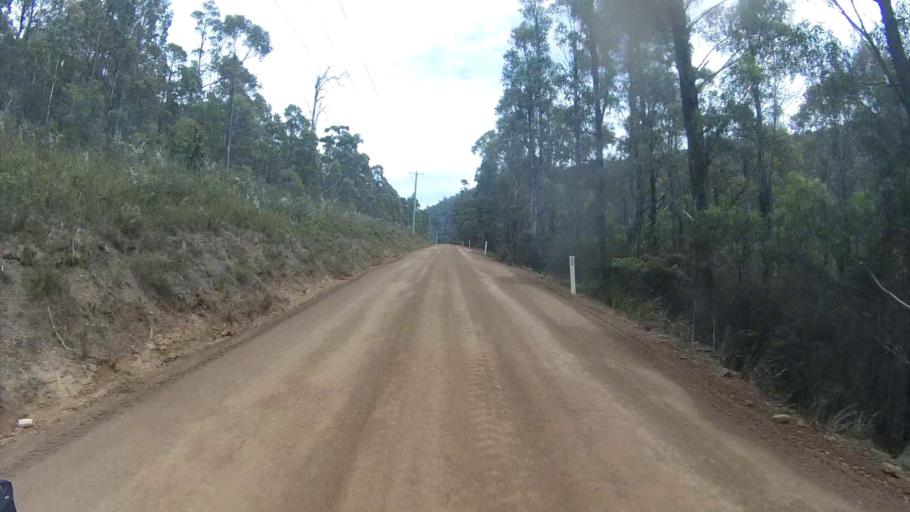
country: AU
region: Tasmania
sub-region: Sorell
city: Sorell
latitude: -42.7470
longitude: 147.7822
